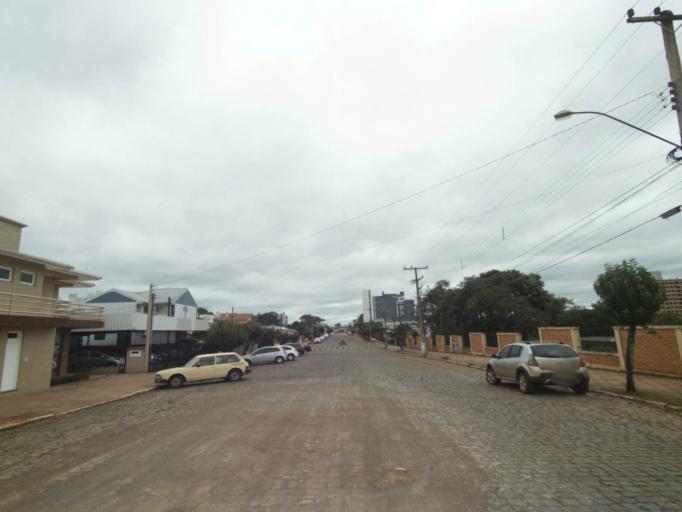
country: BR
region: Rio Grande do Sul
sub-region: Lagoa Vermelha
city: Lagoa Vermelha
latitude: -28.2143
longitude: -51.5183
